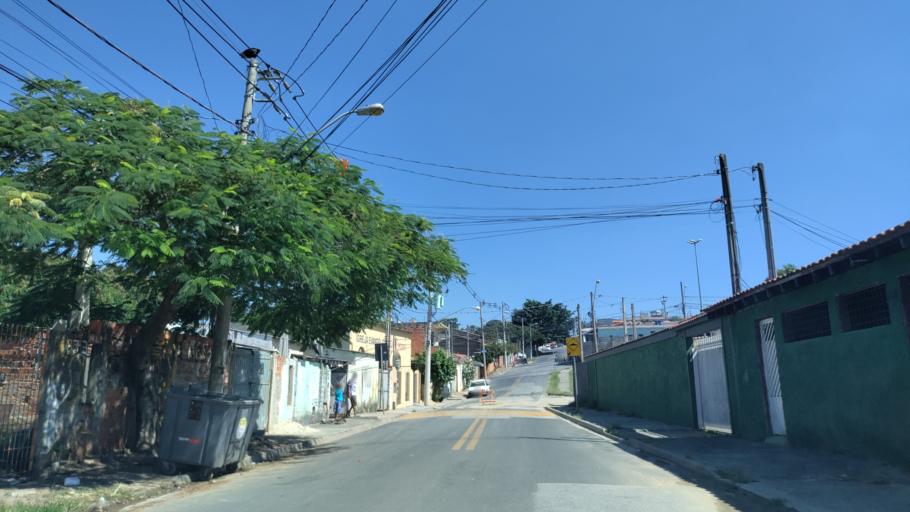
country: BR
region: Sao Paulo
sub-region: Sorocaba
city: Sorocaba
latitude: -23.4685
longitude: -47.4659
